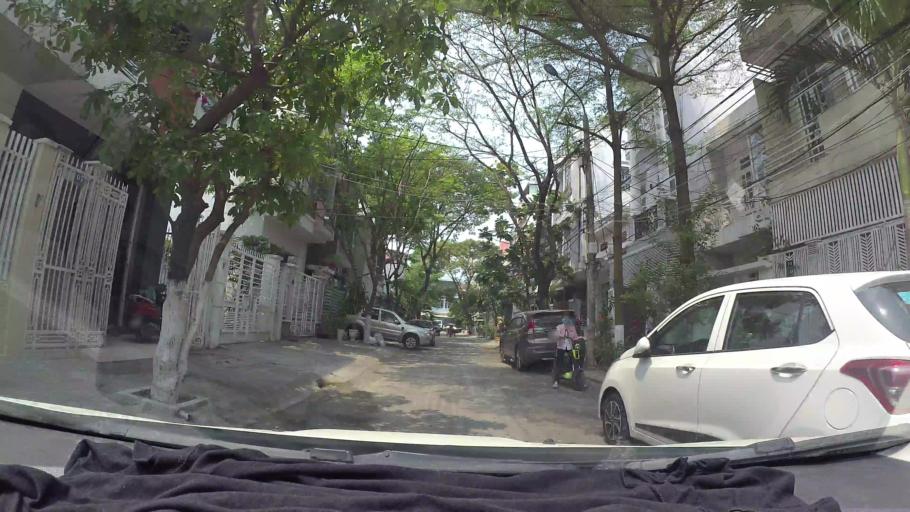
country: VN
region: Da Nang
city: Da Nang
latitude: 16.0802
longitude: 108.2166
